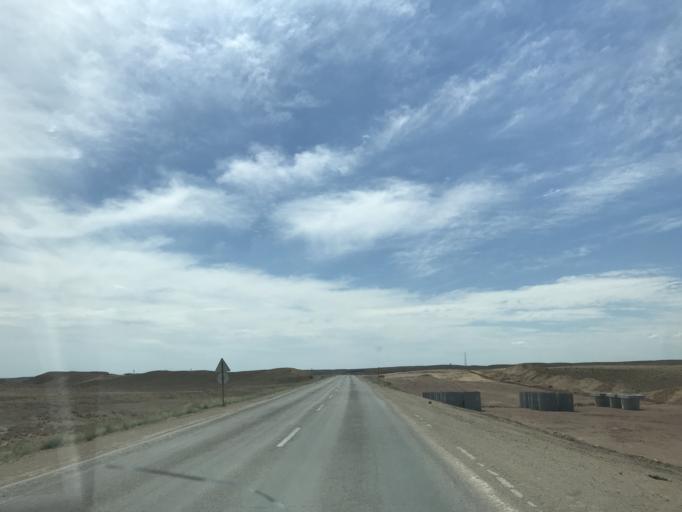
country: KZ
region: Almaty Oblysy
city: Ulken
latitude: 45.0811
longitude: 73.9718
